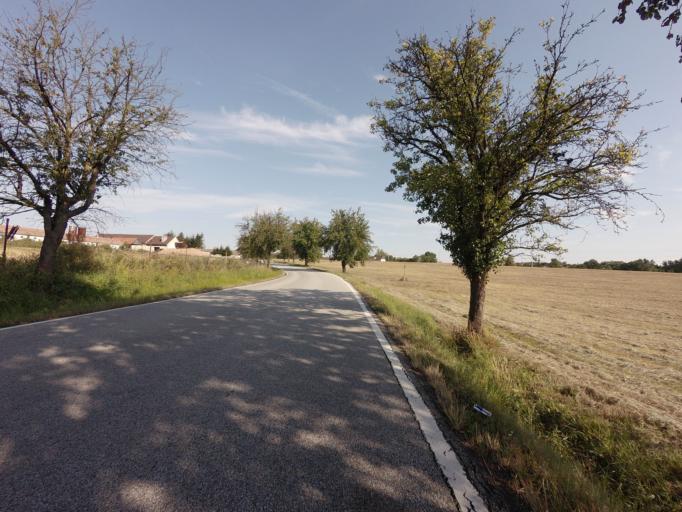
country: CZ
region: Jihocesky
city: Tyn nad Vltavou
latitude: 49.2758
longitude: 14.4016
